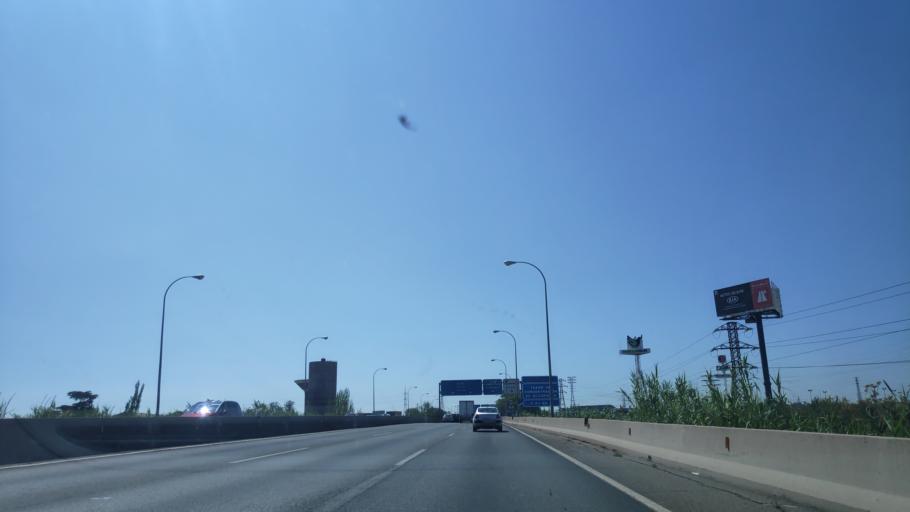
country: ES
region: Madrid
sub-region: Provincia de Madrid
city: Villaverde
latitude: 40.3431
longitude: -3.7239
